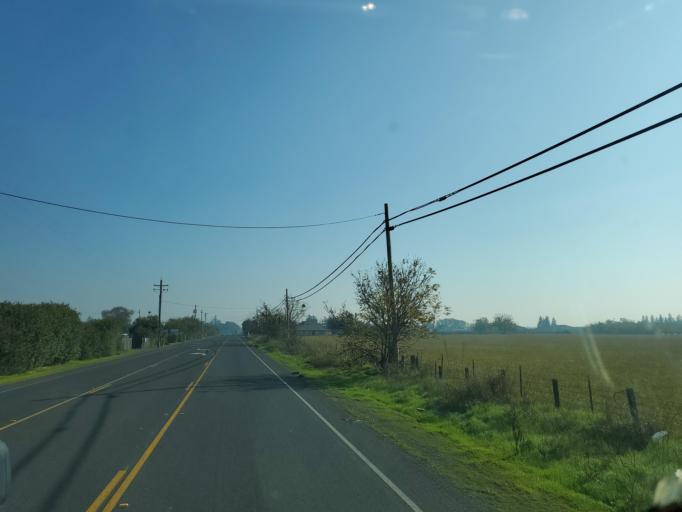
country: US
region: California
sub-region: San Joaquin County
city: French Camp
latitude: 37.8649
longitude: -121.2358
